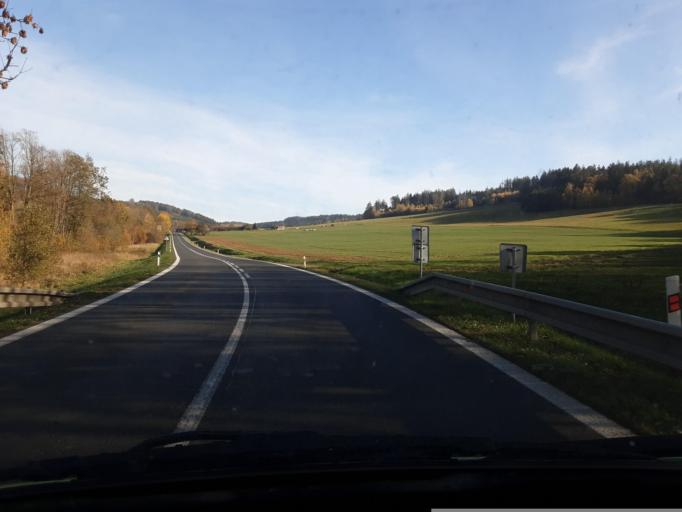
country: CZ
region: Plzensky
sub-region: Okres Klatovy
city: Kolinec
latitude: 49.3580
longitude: 13.3873
